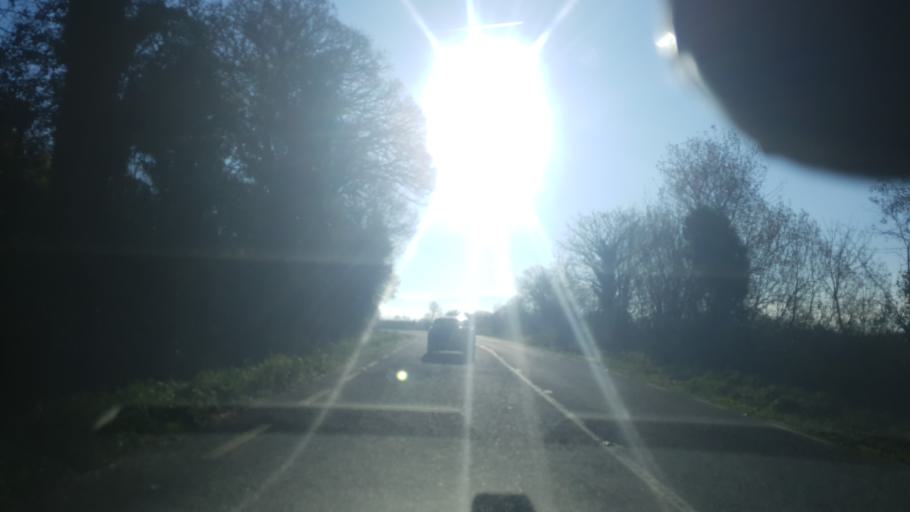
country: IE
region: Munster
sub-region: Ciarrai
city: Cill Airne
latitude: 52.1199
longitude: -9.5207
